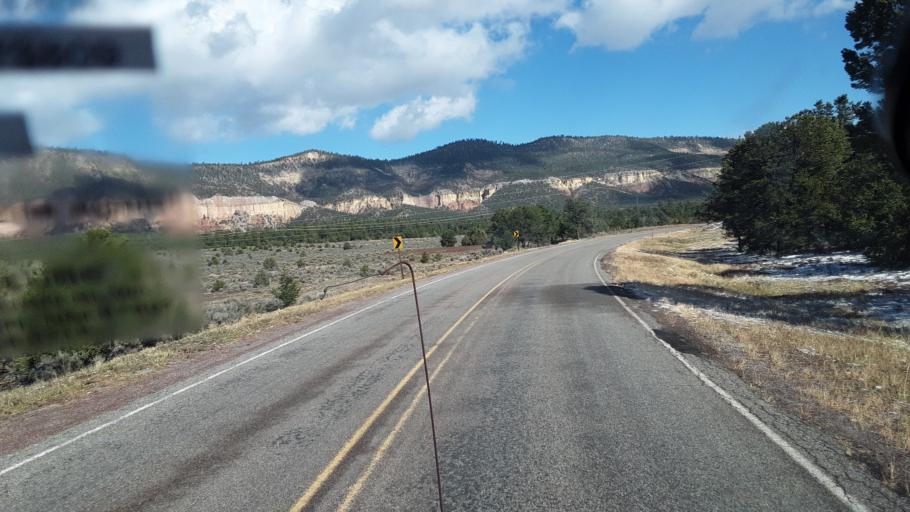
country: US
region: New Mexico
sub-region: Rio Arriba County
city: Santa Teresa
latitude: 36.1987
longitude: -106.7383
